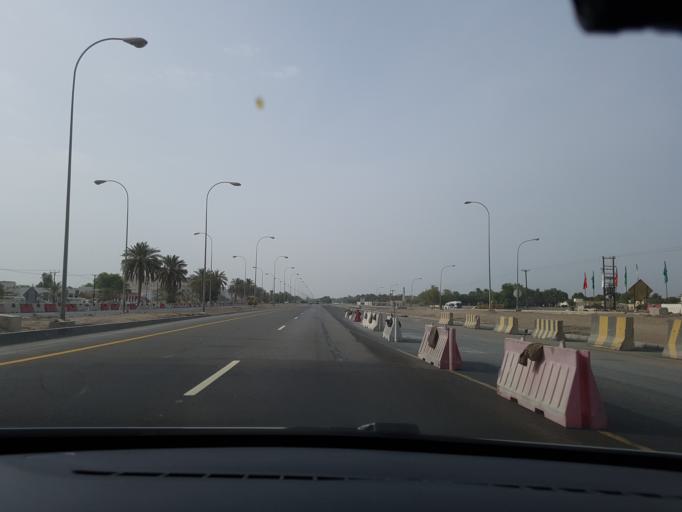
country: OM
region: Al Batinah
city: Al Sohar
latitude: 24.3837
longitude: 56.7013
